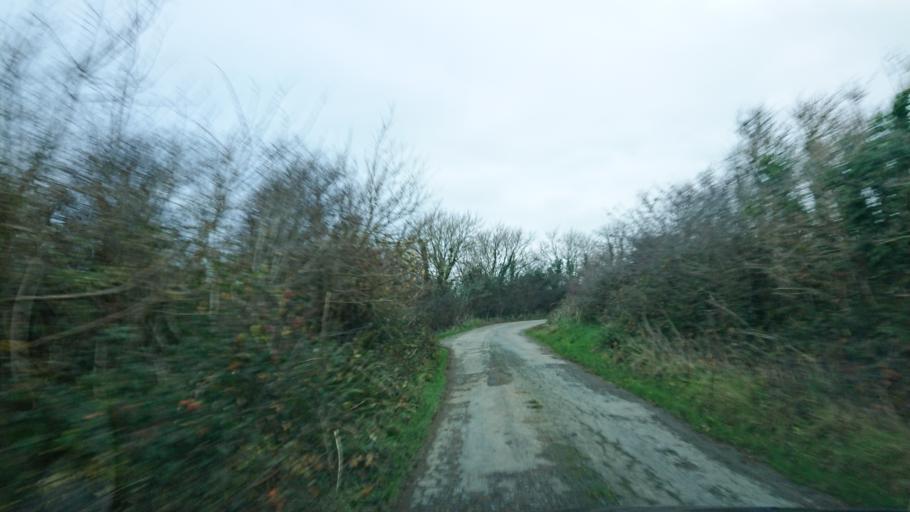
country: IE
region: Munster
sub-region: Waterford
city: Dunmore East
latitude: 52.1881
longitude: -7.0429
